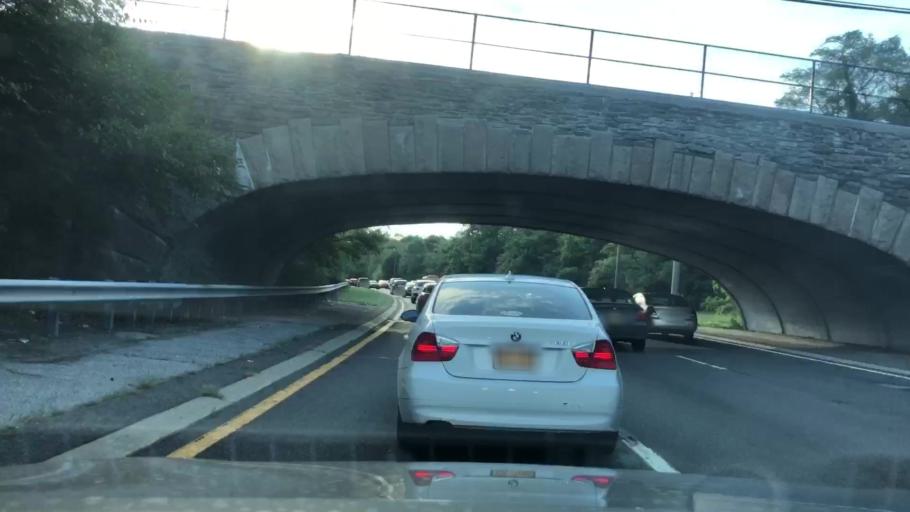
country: US
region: New York
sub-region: Nassau County
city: North Bellmore
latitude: 40.6999
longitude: -73.5299
